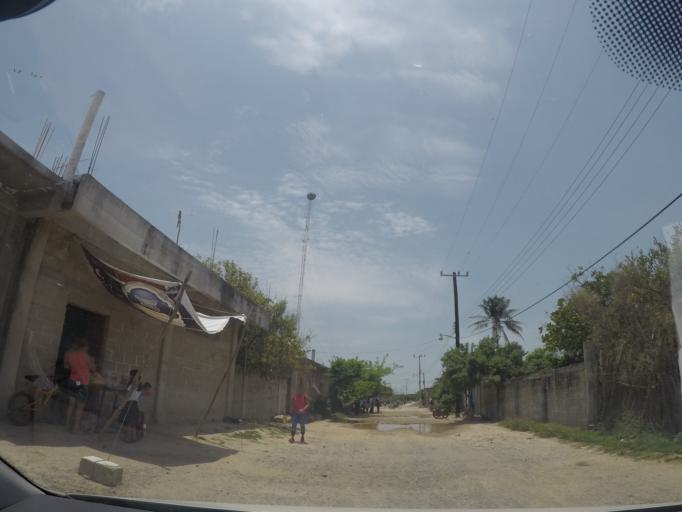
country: MX
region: Oaxaca
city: San Mateo del Mar
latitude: 16.2113
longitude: -94.9817
